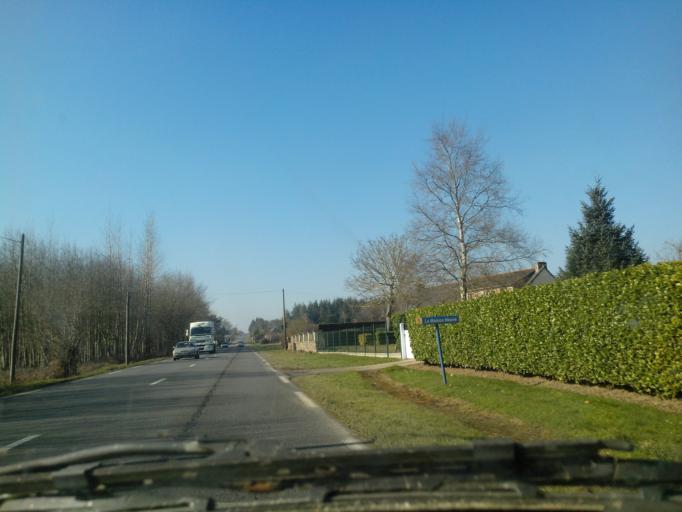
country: FR
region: Brittany
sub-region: Departement des Cotes-d'Armor
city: Merdrignac
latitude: 48.1939
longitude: -2.4487
